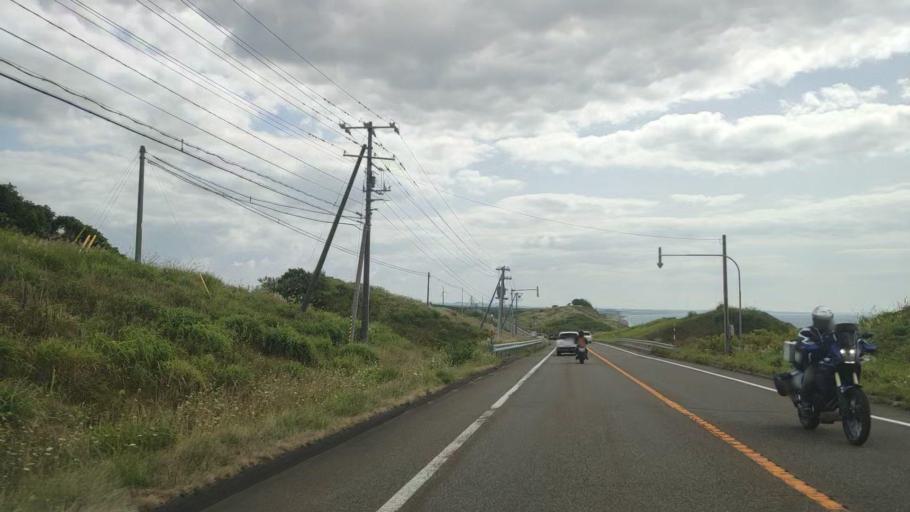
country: JP
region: Hokkaido
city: Rumoi
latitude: 44.5198
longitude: 141.7655
